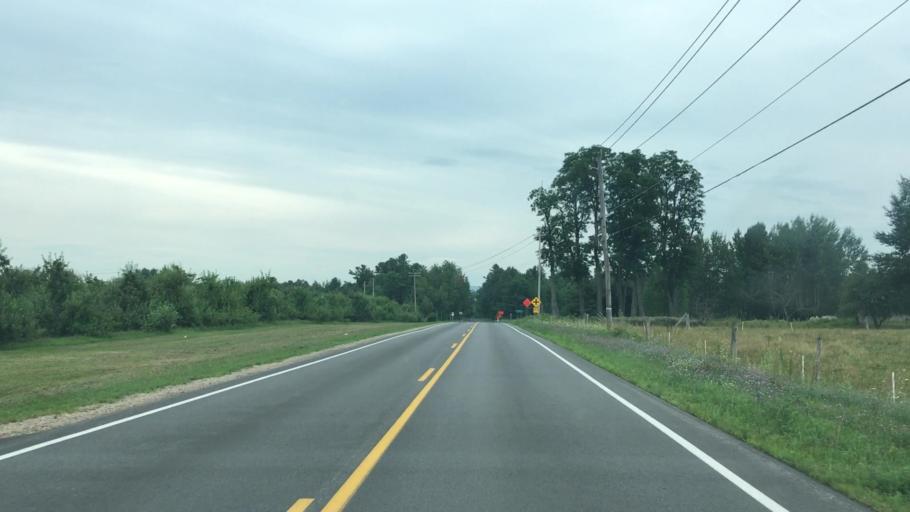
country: US
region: New York
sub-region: Clinton County
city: Peru
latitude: 44.5857
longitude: -73.5711
